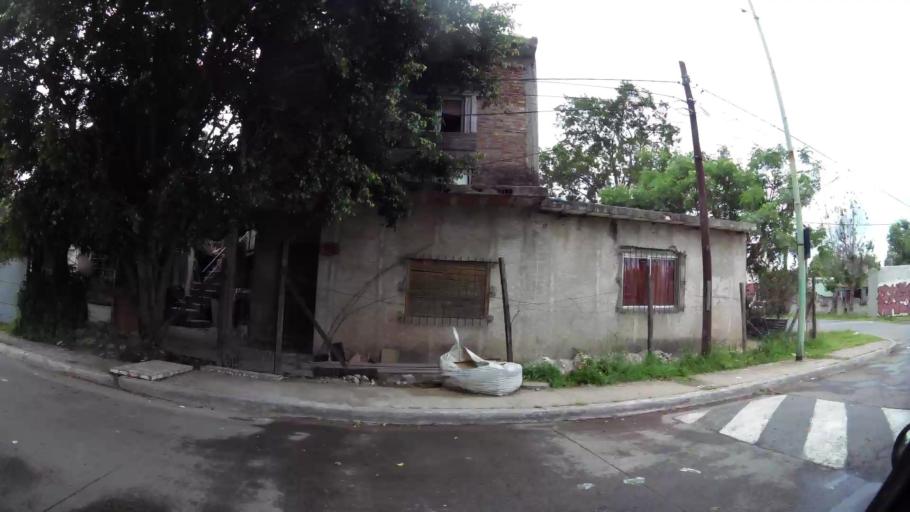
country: AR
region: Buenos Aires
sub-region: Partido de Quilmes
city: Quilmes
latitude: -34.7552
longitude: -58.2275
